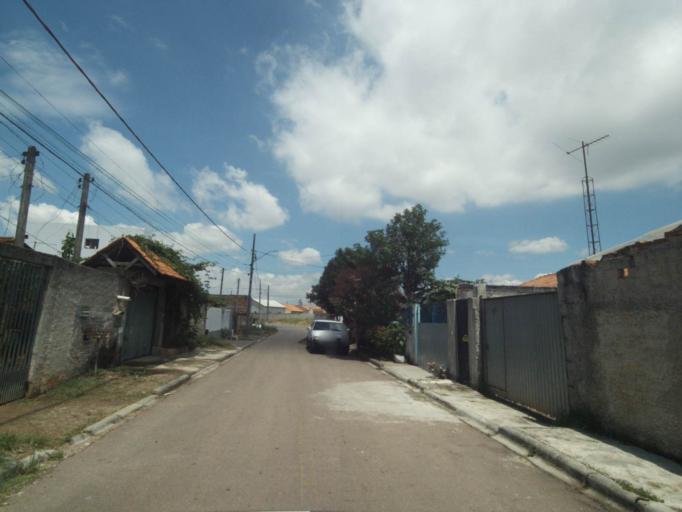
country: BR
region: Parana
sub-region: Pinhais
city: Pinhais
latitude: -25.4707
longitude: -49.1880
